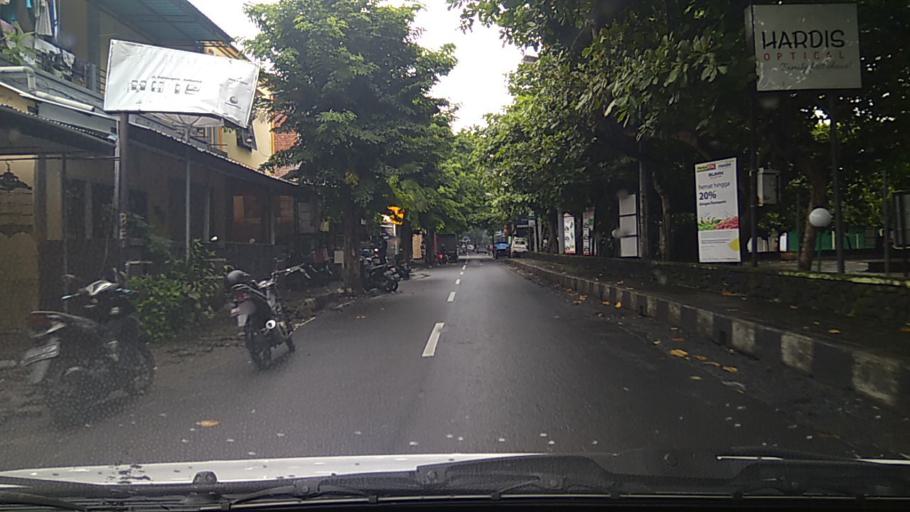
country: ID
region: Bali
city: Karangasem
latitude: -8.4474
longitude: 115.6138
